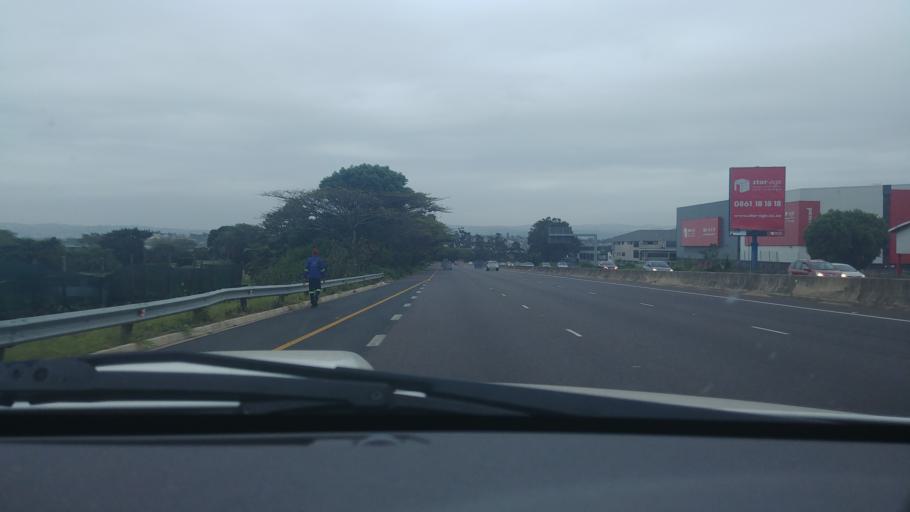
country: ZA
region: KwaZulu-Natal
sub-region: eThekwini Metropolitan Municipality
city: Durban
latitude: -29.7087
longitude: 31.0463
